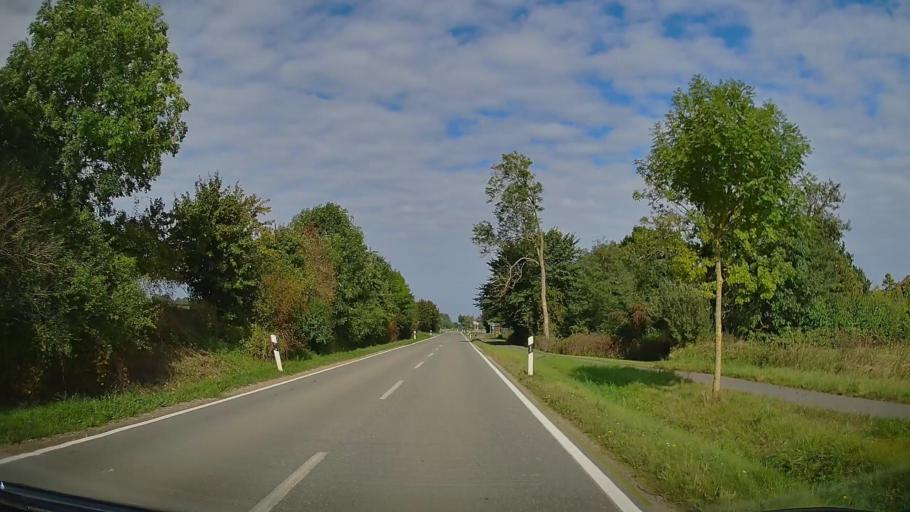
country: DE
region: Schleswig-Holstein
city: Oldenburg in Holstein
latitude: 54.3342
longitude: 10.8926
